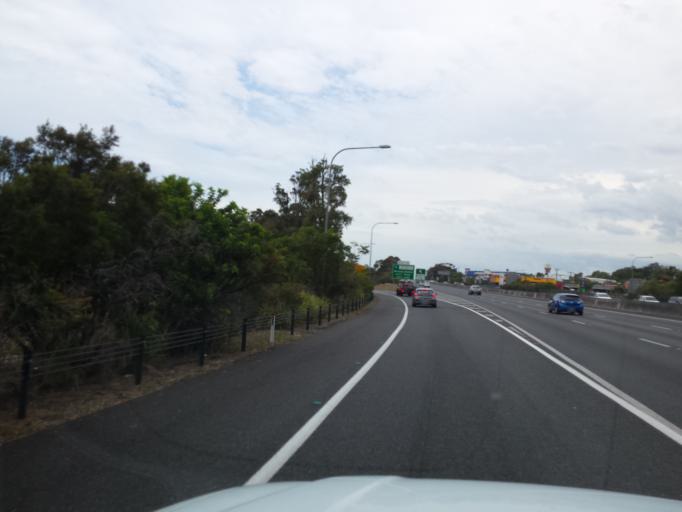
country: AU
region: Queensland
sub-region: Gold Coast
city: Nerang
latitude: -28.0046
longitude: 153.3408
